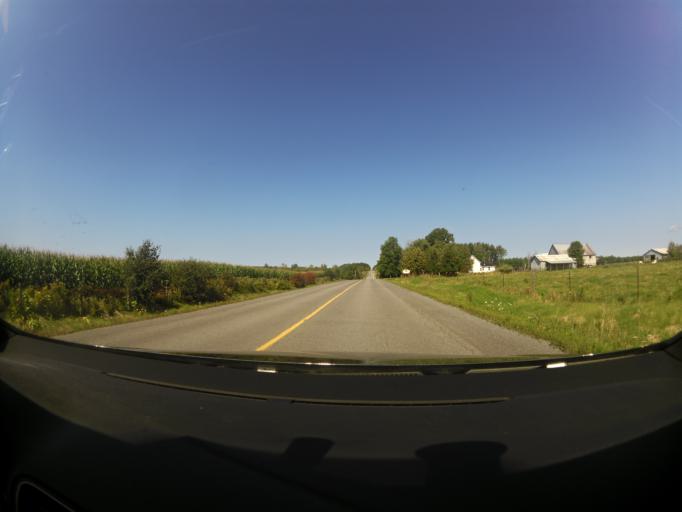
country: CA
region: Ontario
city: Arnprior
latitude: 45.3751
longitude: -76.2630
